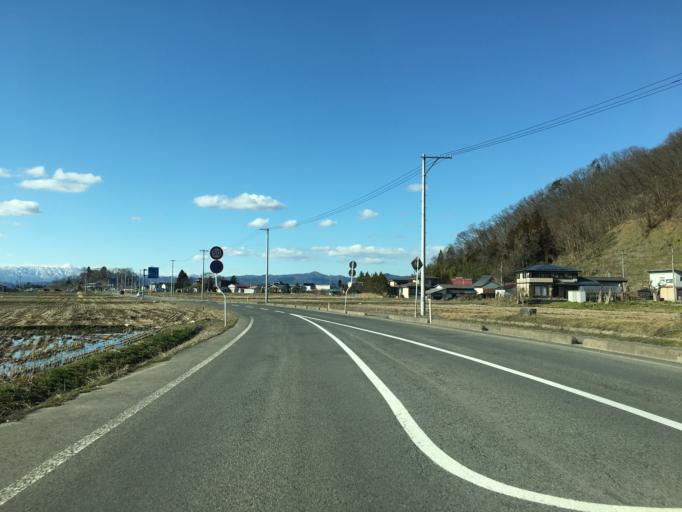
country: JP
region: Yamagata
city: Takahata
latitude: 37.9883
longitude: 140.1827
